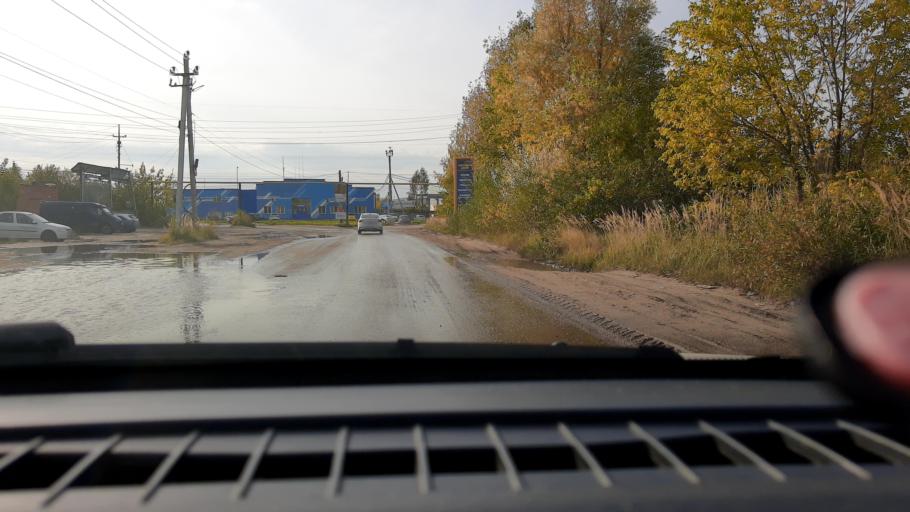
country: RU
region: Nizjnij Novgorod
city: Burevestnik
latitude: 56.1621
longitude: 43.9091
